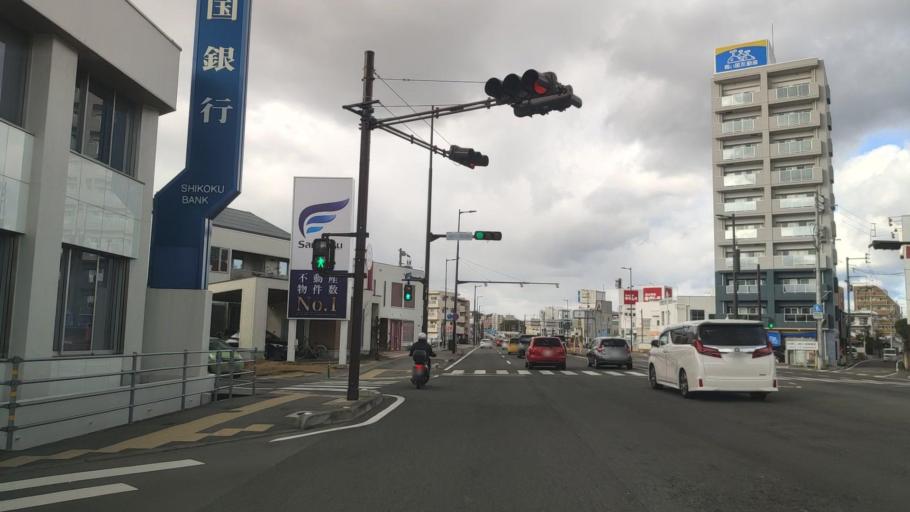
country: JP
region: Ehime
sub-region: Shikoku-chuo Shi
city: Matsuyama
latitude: 33.8296
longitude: 132.7808
